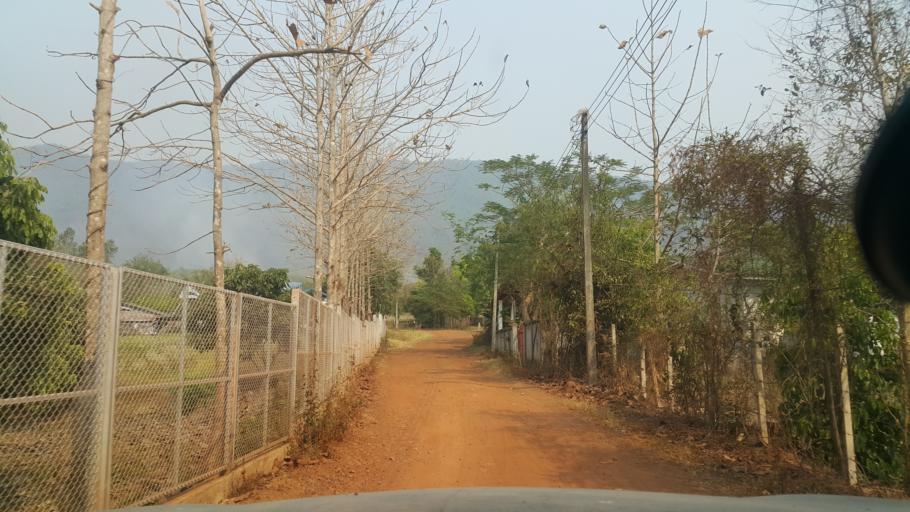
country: TH
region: Chiang Mai
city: Mae On
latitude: 18.7608
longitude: 99.2685
